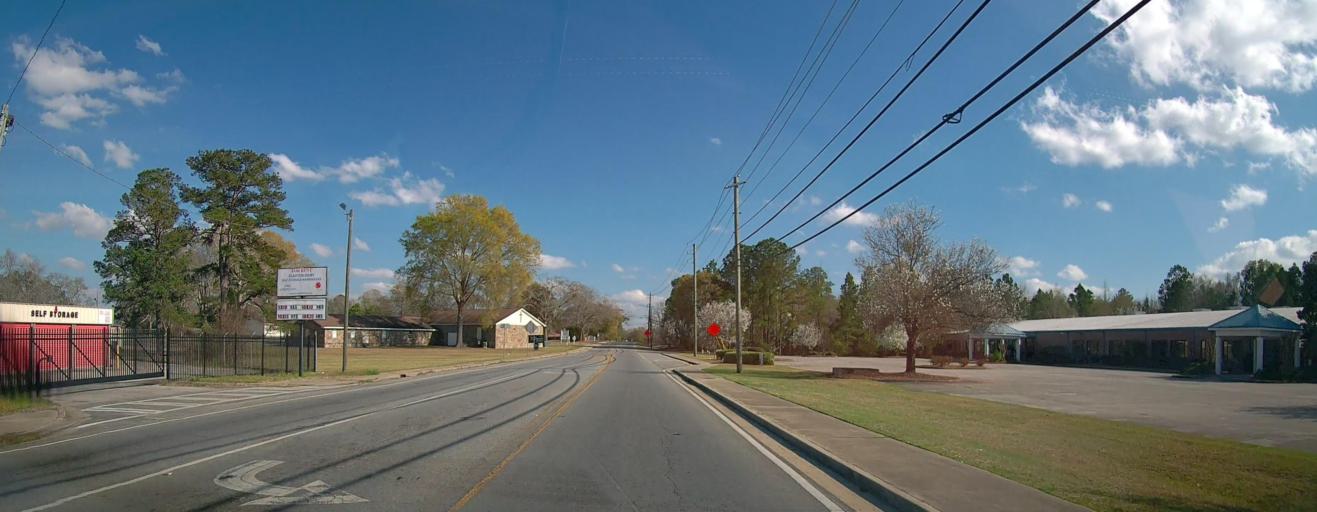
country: US
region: Georgia
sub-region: Laurens County
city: Dublin
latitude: 32.5447
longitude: -82.9208
